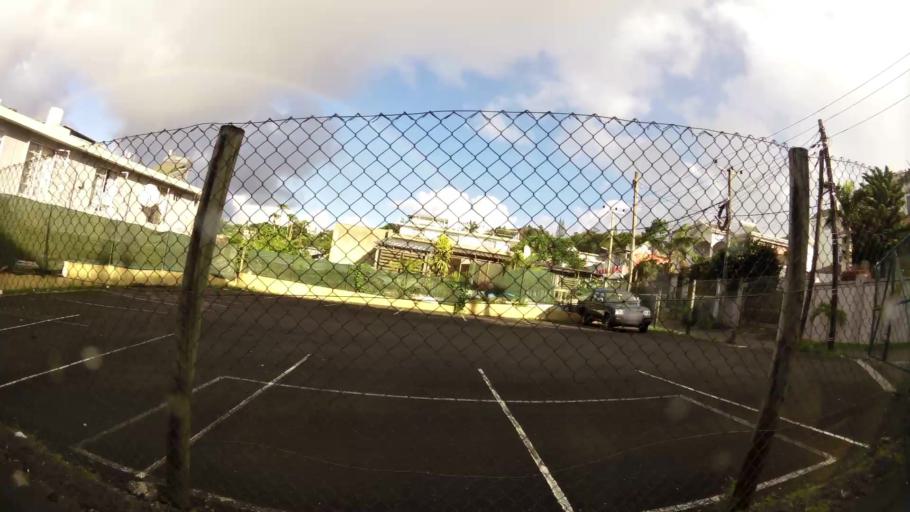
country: MU
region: Plaines Wilhems
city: Curepipe
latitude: -20.3136
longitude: 57.5101
